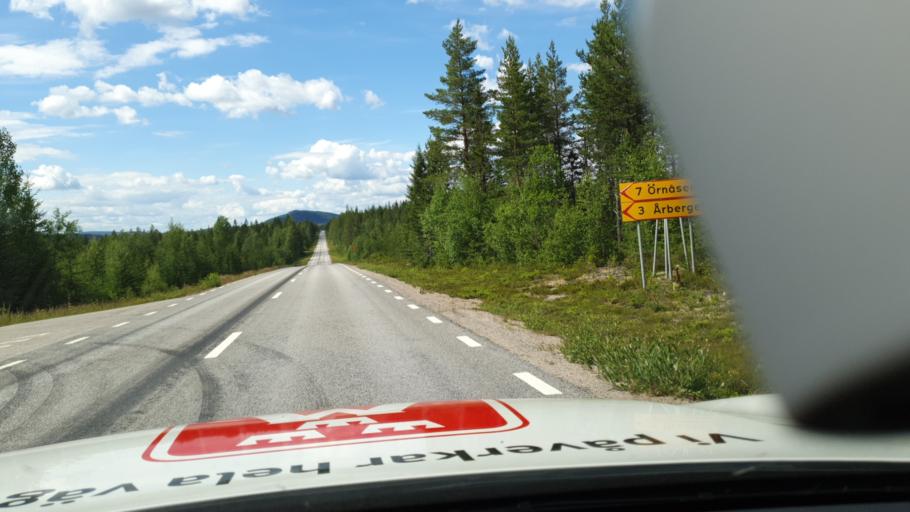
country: SE
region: Jaemtland
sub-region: Harjedalens Kommun
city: Sveg
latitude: 61.9823
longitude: 15.0695
